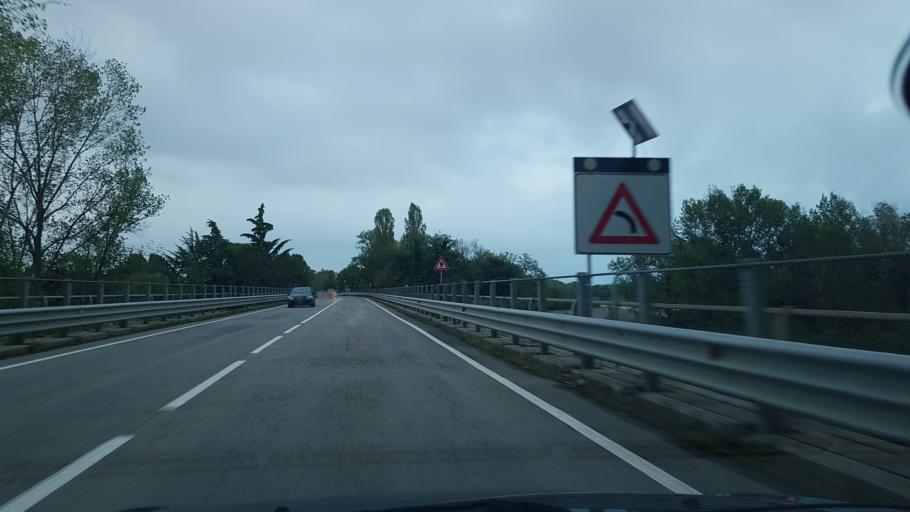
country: IT
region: Friuli Venezia Giulia
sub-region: Provincia di Gorizia
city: Medea
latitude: 45.8940
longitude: 13.4060
